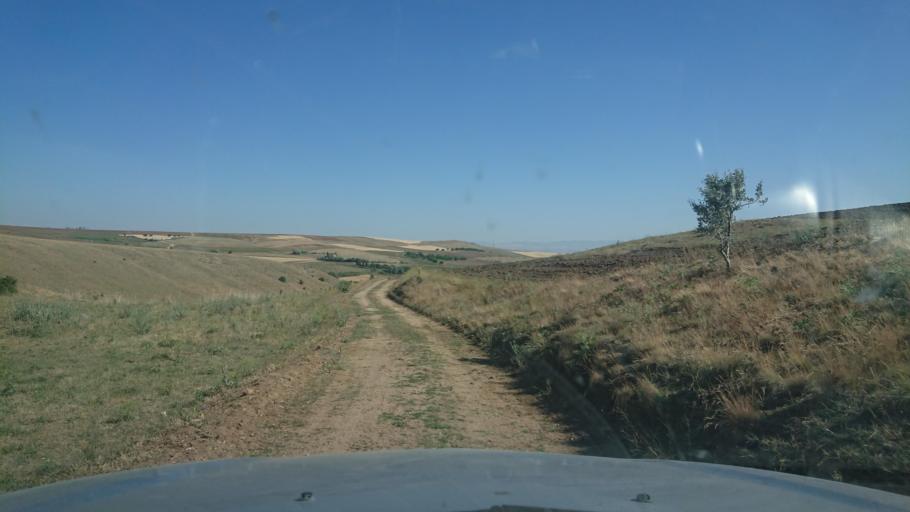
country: TR
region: Aksaray
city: Agacoren
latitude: 38.8367
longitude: 33.9269
